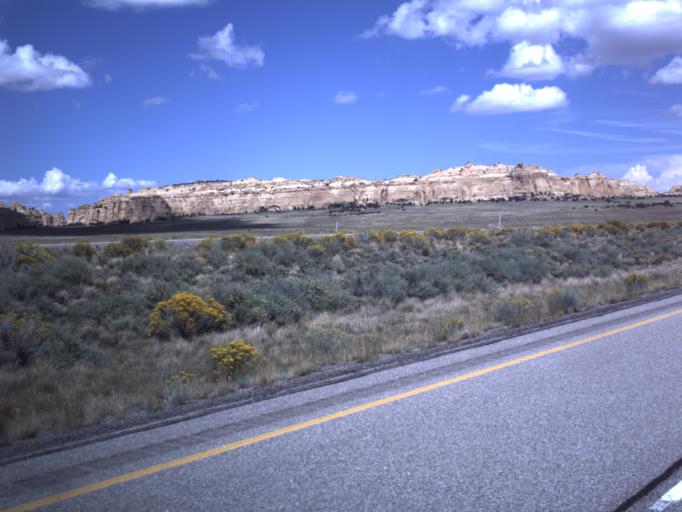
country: US
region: Utah
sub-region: Emery County
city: Ferron
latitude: 38.8662
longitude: -110.7867
